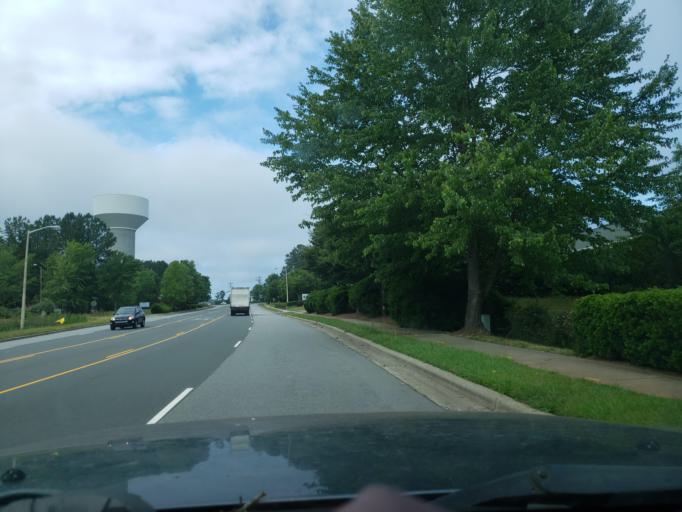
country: US
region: North Carolina
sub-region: Durham County
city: Gorman
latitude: 35.9306
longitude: -78.8114
